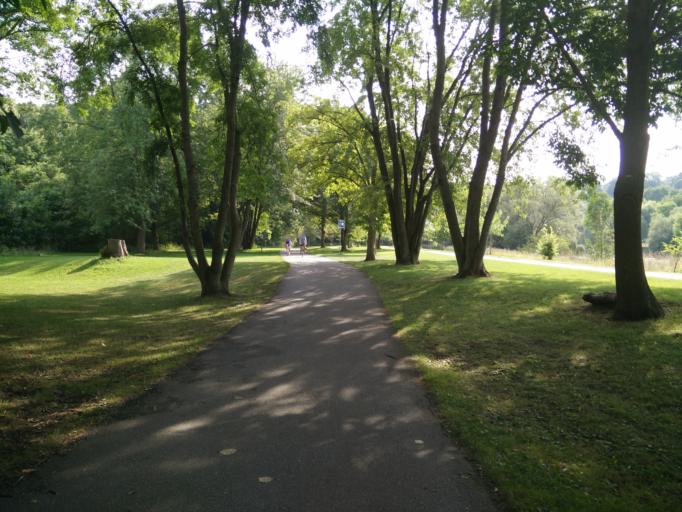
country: CA
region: Ontario
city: Etobicoke
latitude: 43.6574
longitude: -79.4991
